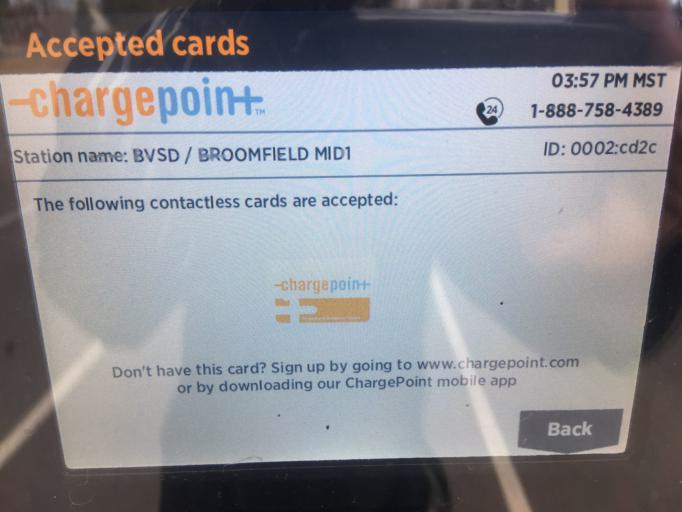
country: US
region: Colorado
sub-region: Broomfield County
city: Broomfield
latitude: 39.9381
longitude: -105.0778
